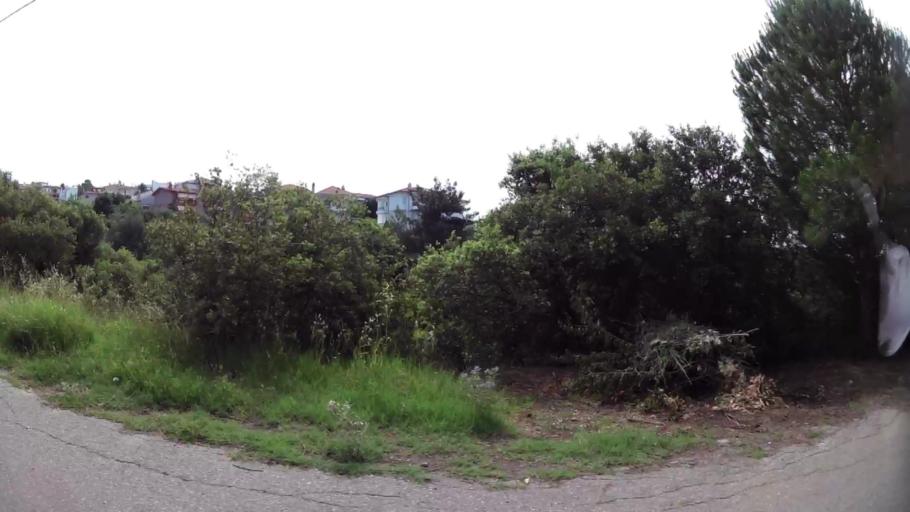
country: GR
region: Central Macedonia
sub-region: Nomos Thessalonikis
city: Panorama
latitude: 40.5748
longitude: 23.0084
